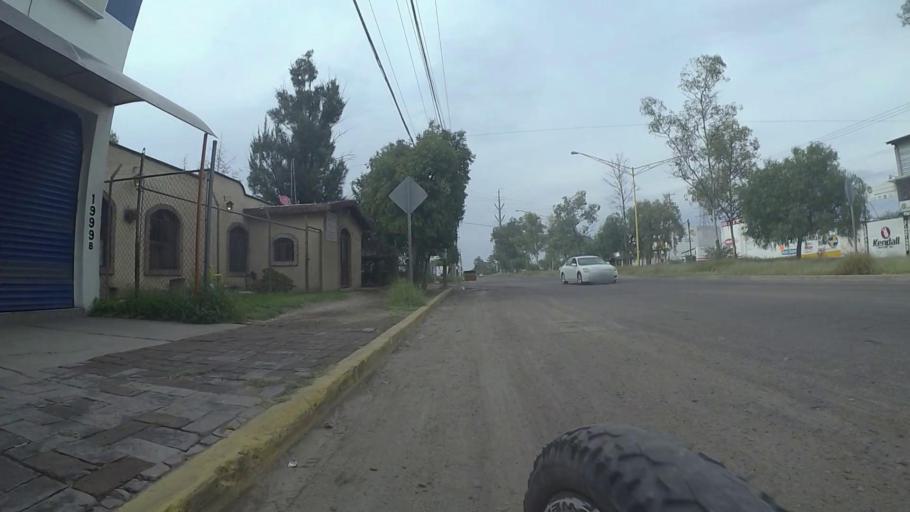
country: MX
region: Aguascalientes
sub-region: Aguascalientes
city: San Sebastian [Fraccionamiento]
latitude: 21.8340
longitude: -102.2937
